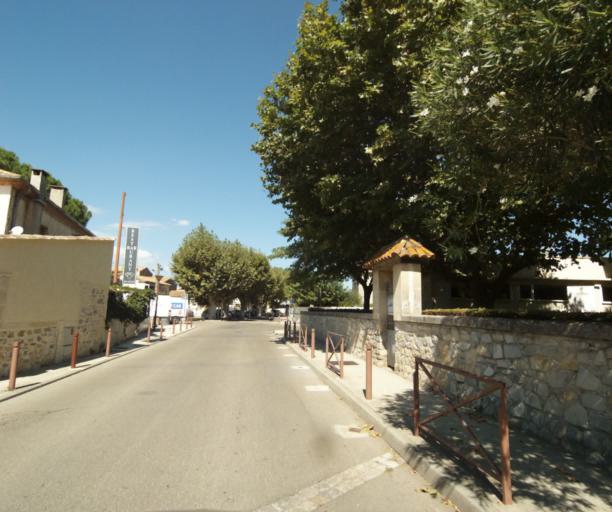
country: FR
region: Languedoc-Roussillon
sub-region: Departement du Gard
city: Rodilhan
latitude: 43.8264
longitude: 4.4304
